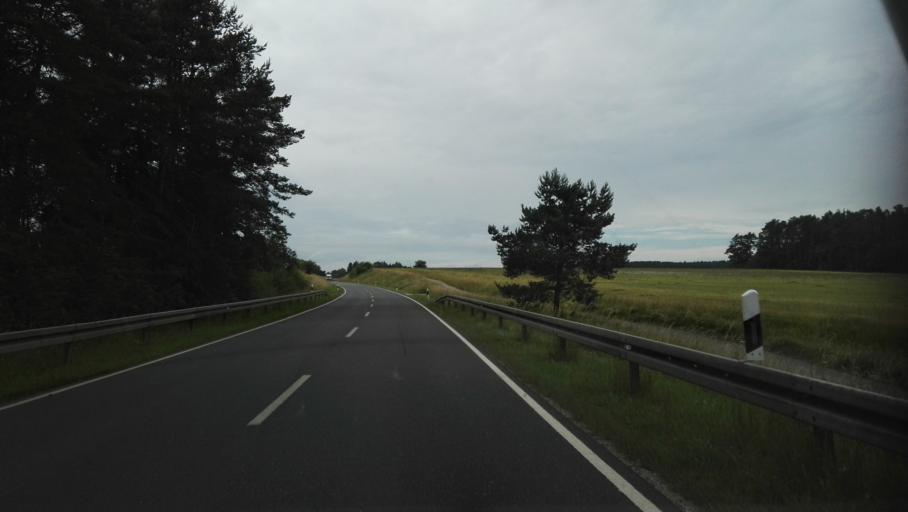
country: DE
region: Bavaria
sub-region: Upper Franconia
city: Hollfeld
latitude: 49.9185
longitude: 11.3100
